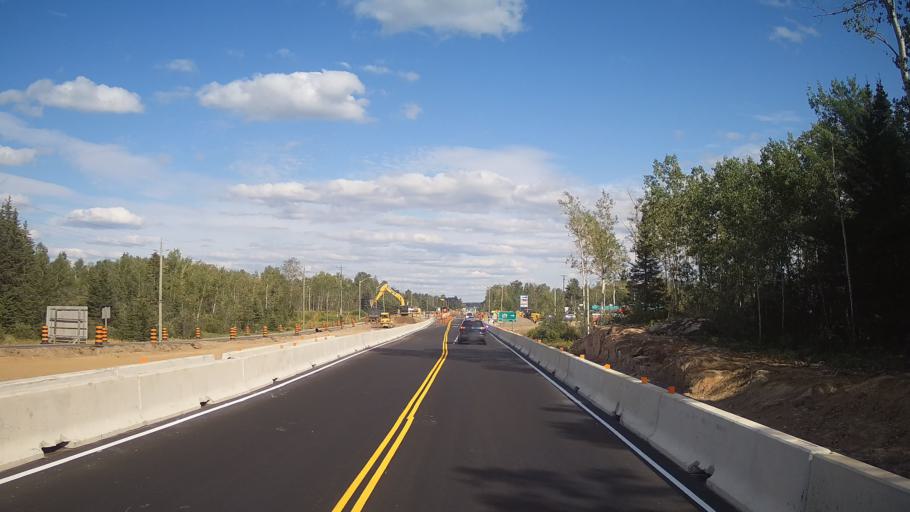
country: CA
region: Ontario
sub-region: Nipissing District
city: North Bay
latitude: 46.2816
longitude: -79.3052
